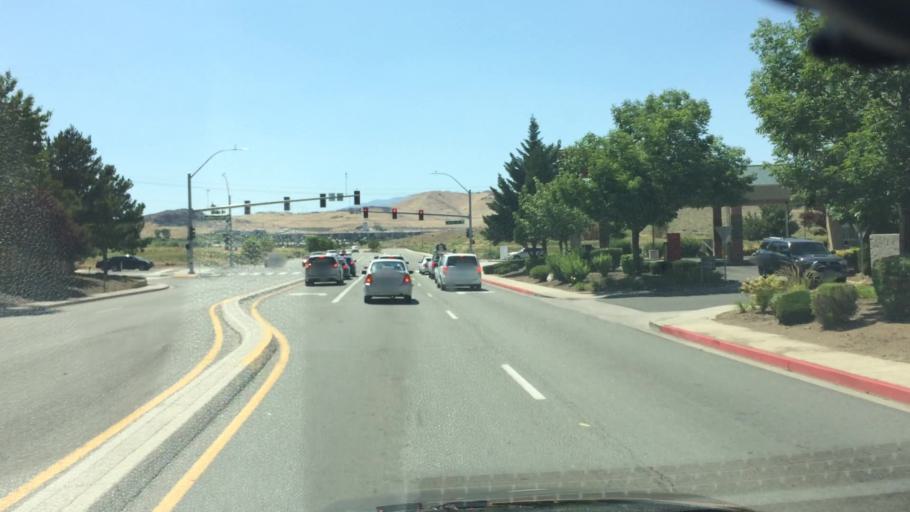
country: US
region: Nevada
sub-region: Washoe County
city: Sparks
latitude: 39.5767
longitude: -119.7230
